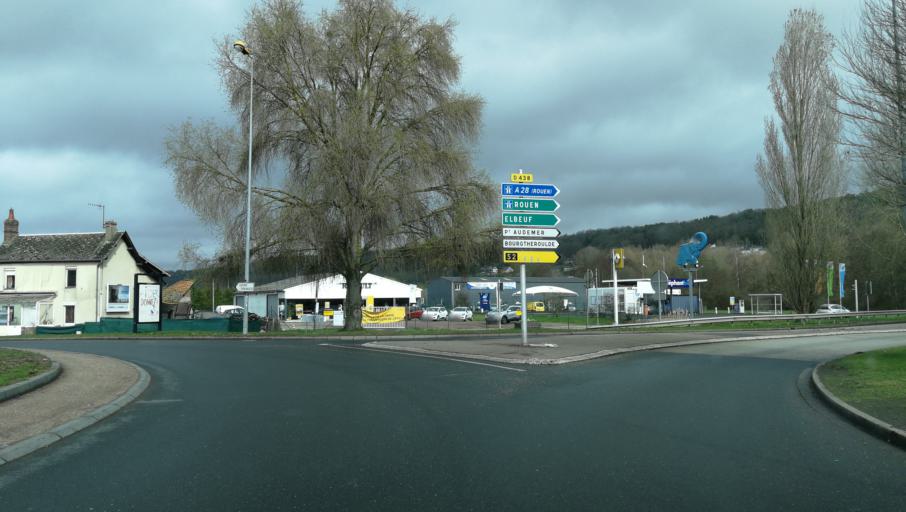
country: FR
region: Haute-Normandie
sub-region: Departement de l'Eure
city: Brionne
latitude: 49.2000
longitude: 0.7161
